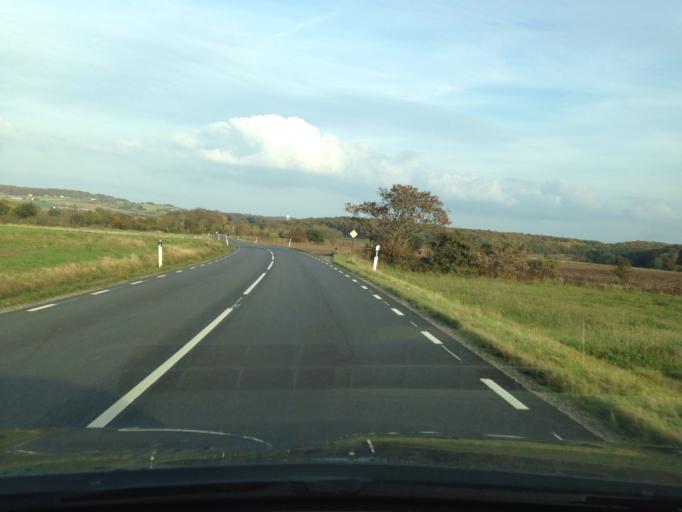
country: SE
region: Skane
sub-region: Angelholms Kommun
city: Vejbystrand
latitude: 56.4341
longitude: 12.6799
